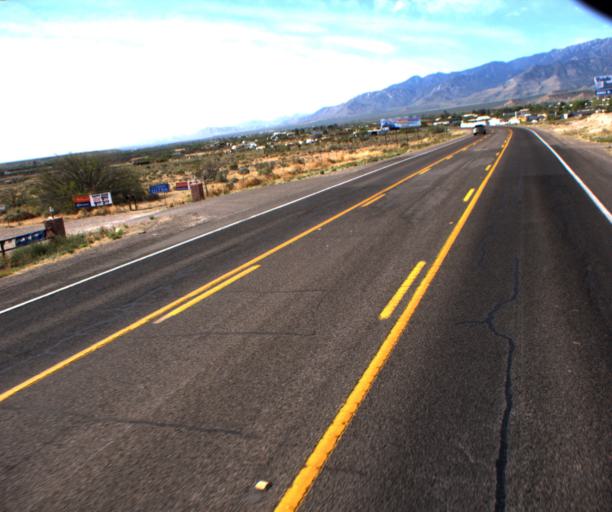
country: US
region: Arizona
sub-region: Graham County
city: Cactus Flat
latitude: 32.7828
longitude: -109.7138
